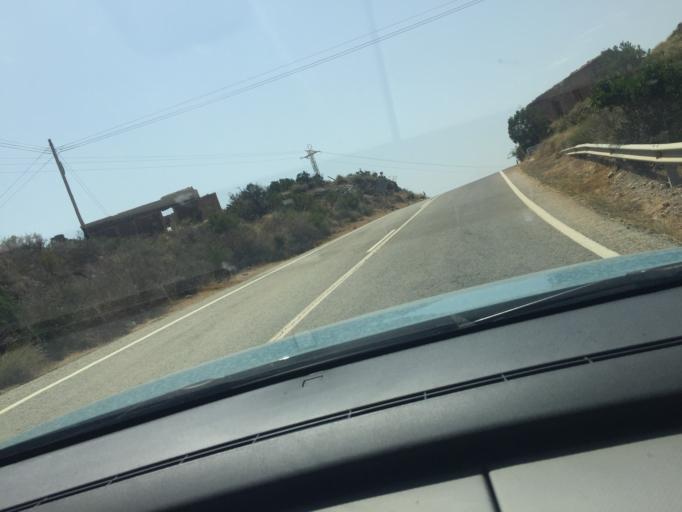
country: ES
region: Murcia
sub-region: Murcia
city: La Union
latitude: 37.5877
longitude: -0.8724
